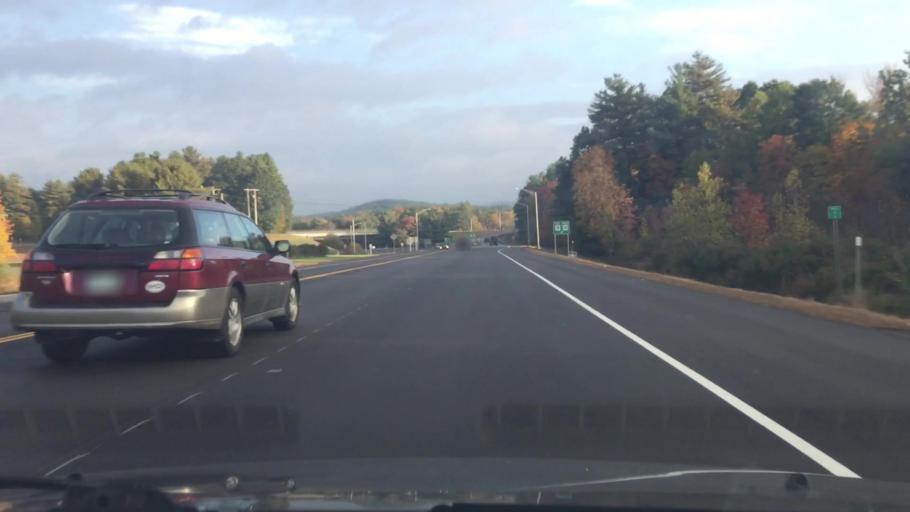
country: US
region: New Hampshire
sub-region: Cheshire County
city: Keene
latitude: 42.9403
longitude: -72.2957
